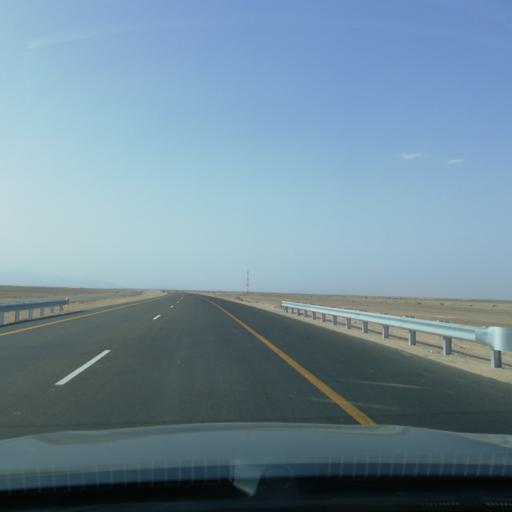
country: OM
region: Muhafazat ad Dakhiliyah
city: Adam
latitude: 22.1327
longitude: 57.5254
